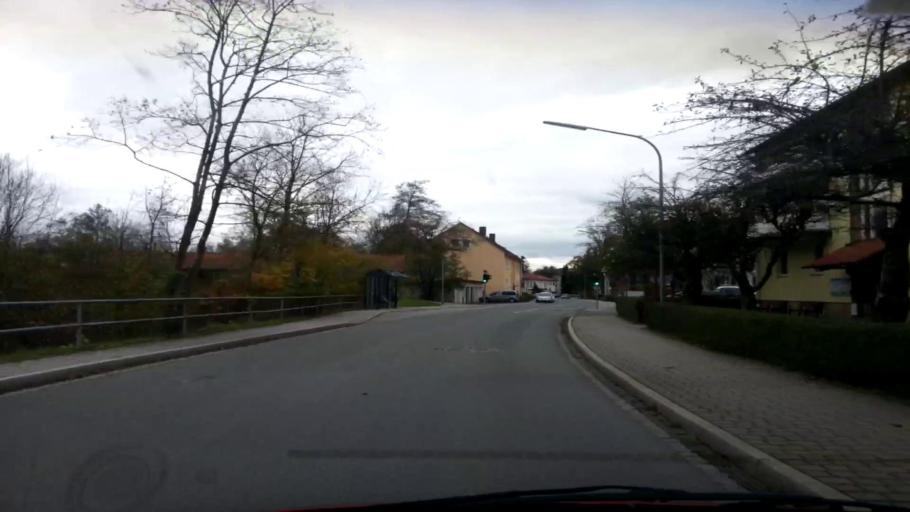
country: DE
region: Bavaria
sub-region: Upper Franconia
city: Kronach
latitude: 50.2443
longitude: 11.3341
